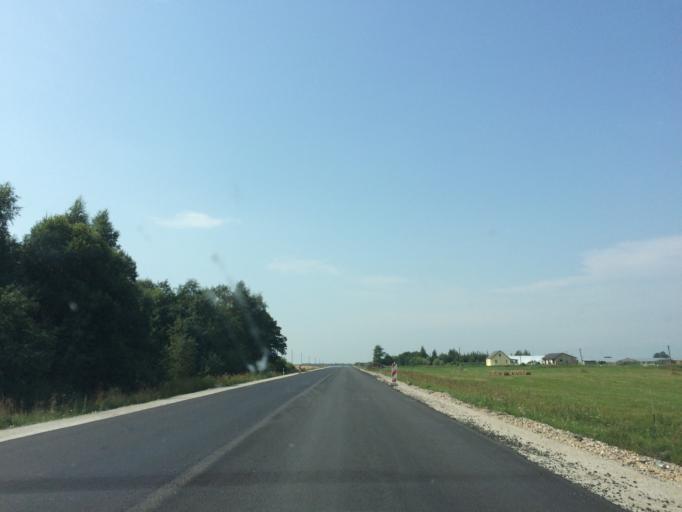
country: LV
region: Ludzas Rajons
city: Ludza
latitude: 56.5279
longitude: 27.5346
